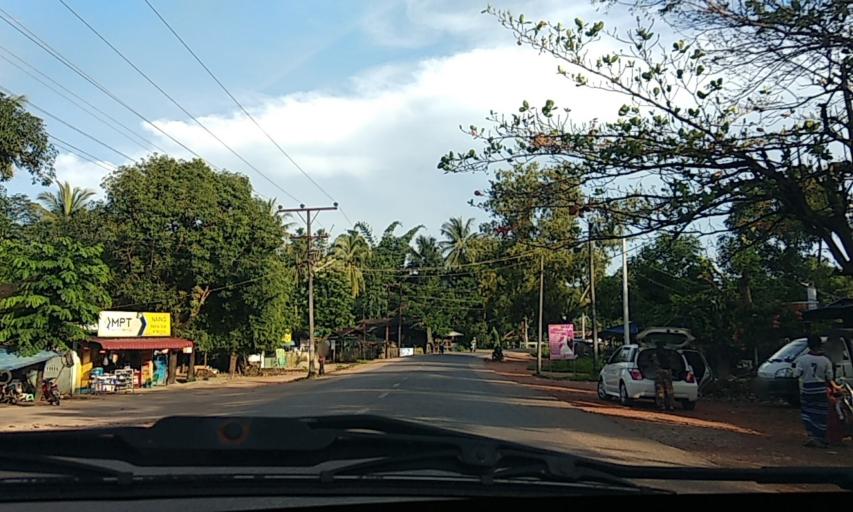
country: MM
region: Mon
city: Mawlamyine
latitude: 16.4109
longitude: 97.6999
